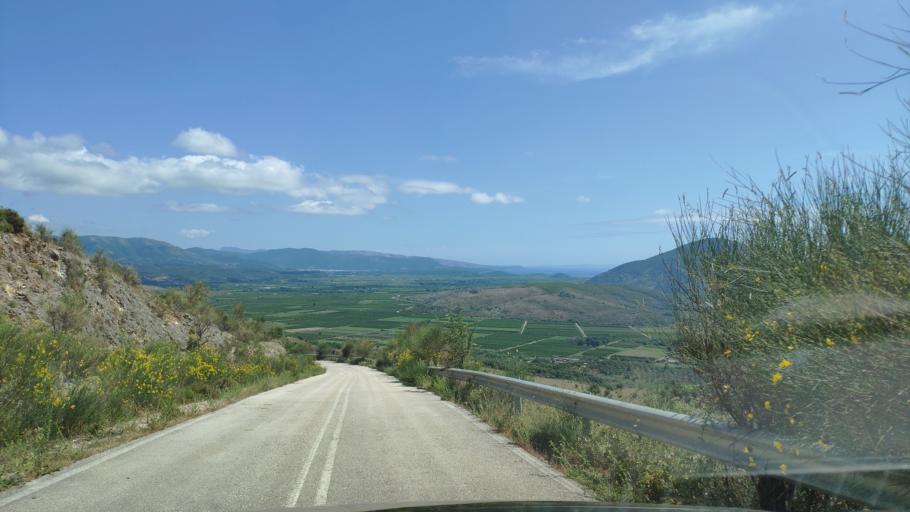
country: AL
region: Vlore
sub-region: Rrethi i Sarandes
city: Konispol
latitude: 39.6333
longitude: 20.2057
